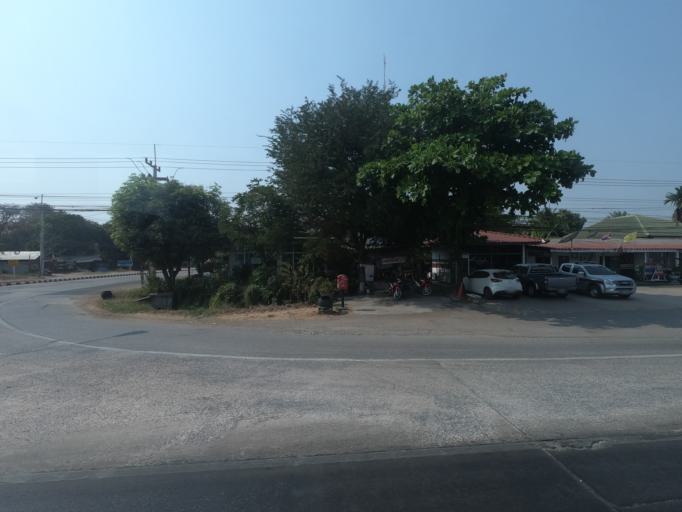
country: TH
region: Nakhon Ratchasima
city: Non Daeng
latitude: 15.3440
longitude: 102.4438
